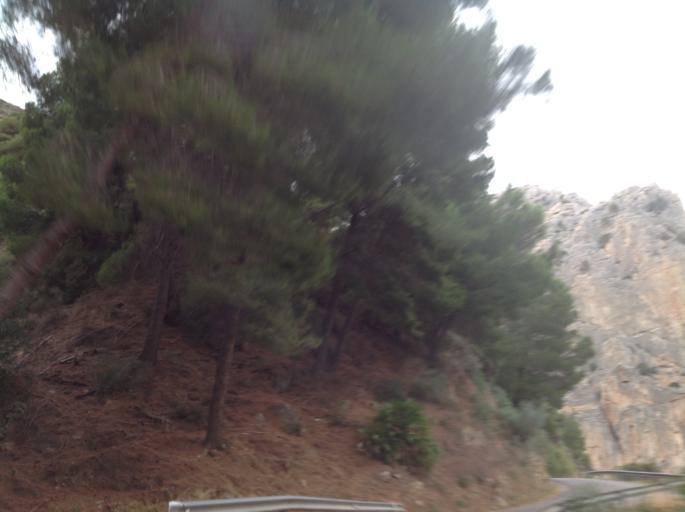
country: ES
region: Andalusia
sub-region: Provincia de Malaga
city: Carratraca
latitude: 36.9128
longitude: -4.7710
